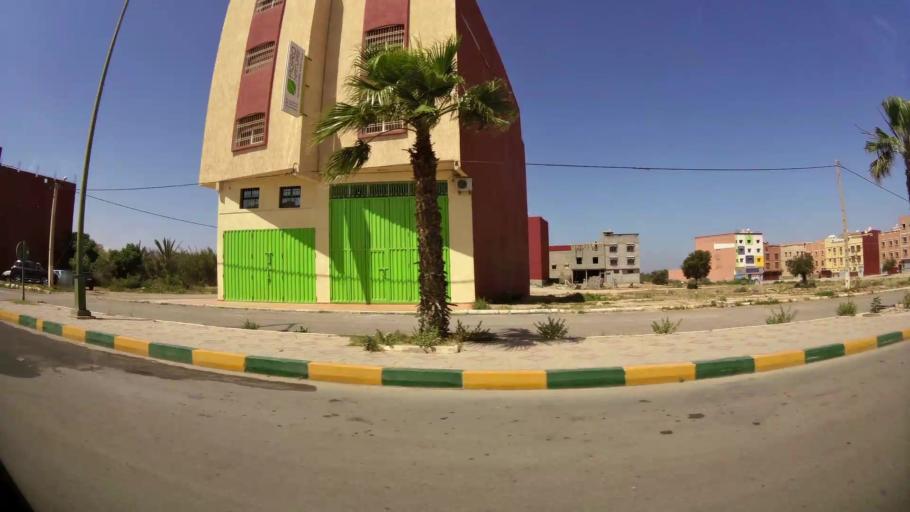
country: MA
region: Souss-Massa-Draa
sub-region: Inezgane-Ait Mellou
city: Inezgane
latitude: 30.3119
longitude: -9.5029
